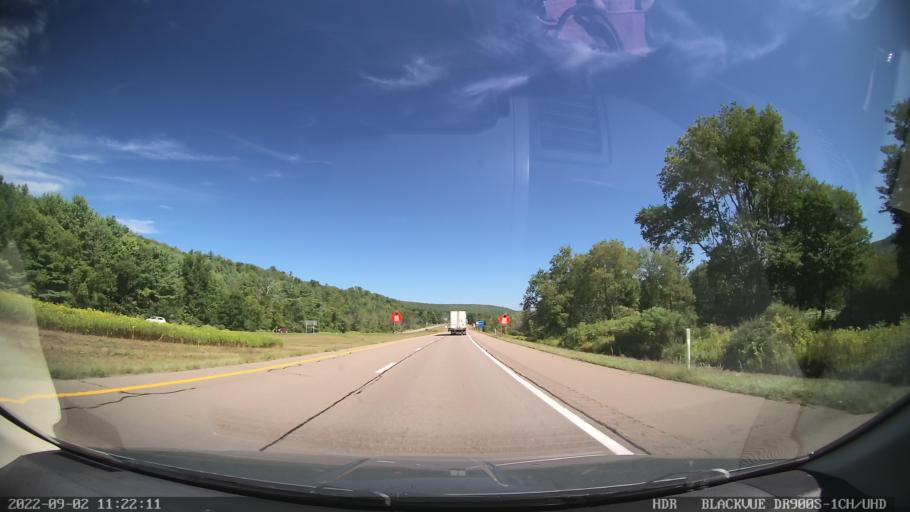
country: US
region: New York
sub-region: Steuben County
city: Gang Mills
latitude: 42.0959
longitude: -77.1583
